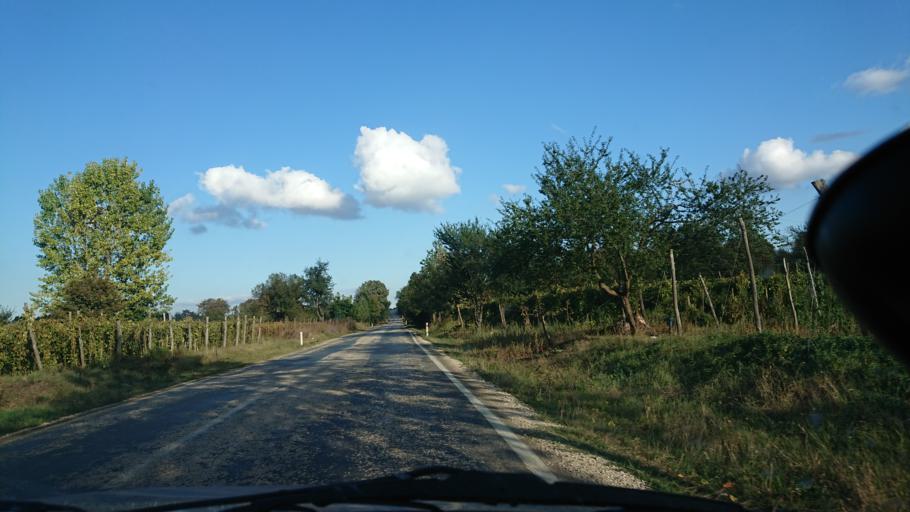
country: TR
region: Bilecik
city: Pazaryeri
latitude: 40.0149
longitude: 29.8445
